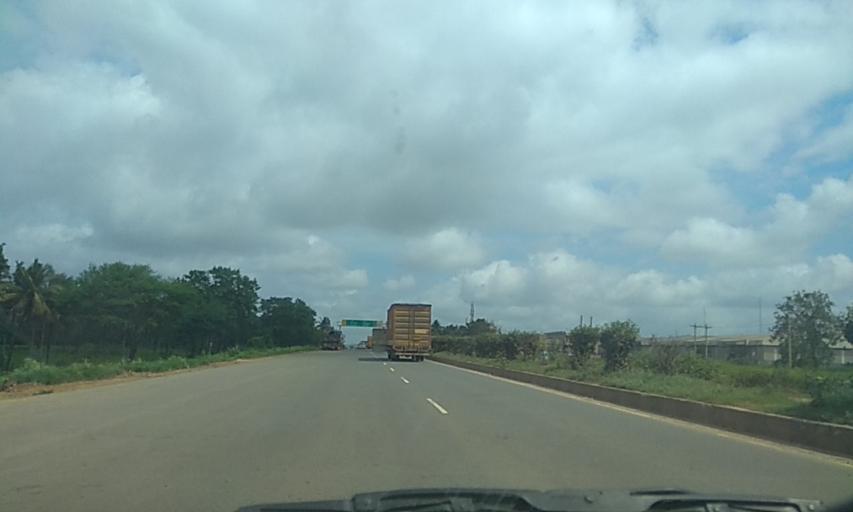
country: IN
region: Karnataka
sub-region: Dharwad
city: Hubli
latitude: 15.3115
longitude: 75.1449
